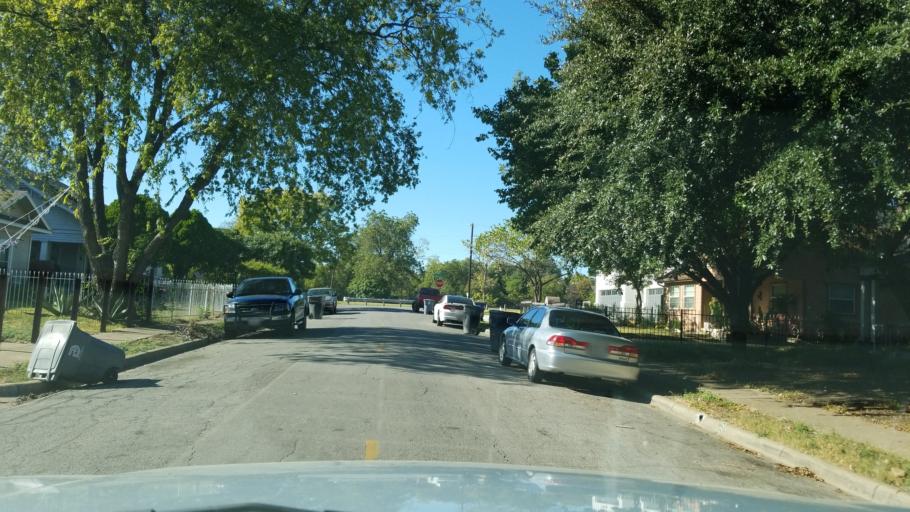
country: US
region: Texas
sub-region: Dallas County
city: Highland Park
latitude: 32.8003
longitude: -96.7517
